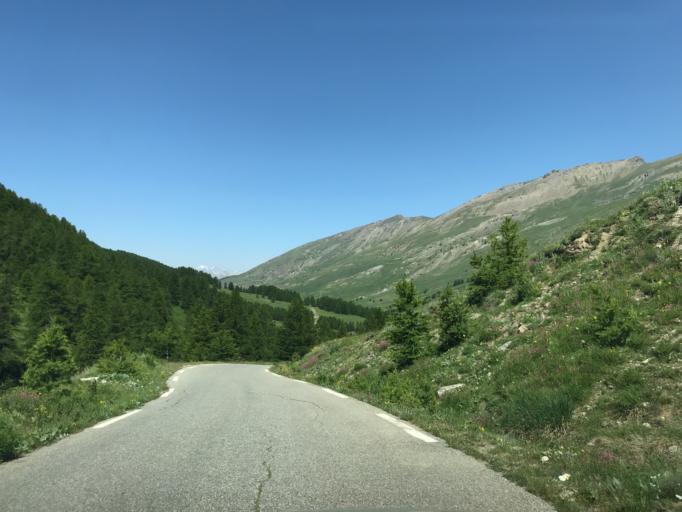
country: IT
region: Piedmont
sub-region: Provincia di Cuneo
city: Pontechianale
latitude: 44.7084
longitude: 6.9243
